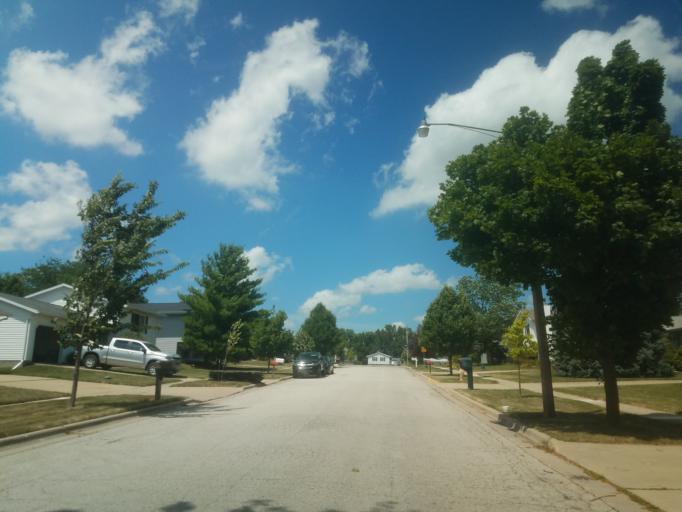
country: US
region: Illinois
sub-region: McLean County
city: Bloomington
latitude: 40.4454
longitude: -89.0305
